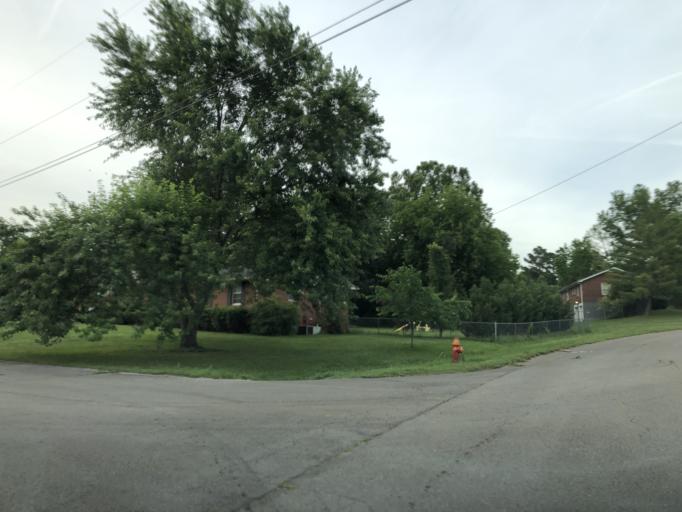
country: US
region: Tennessee
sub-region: Davidson County
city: Goodlettsville
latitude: 36.2891
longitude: -86.7152
